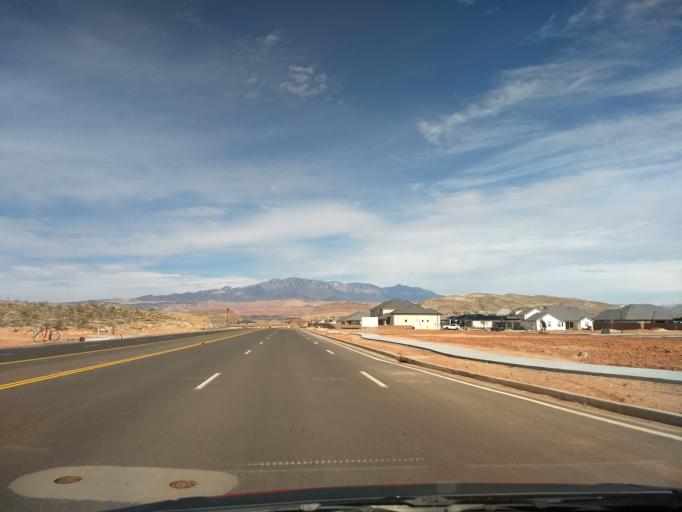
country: US
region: Utah
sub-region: Washington County
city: Washington
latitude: 37.0717
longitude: -113.4942
